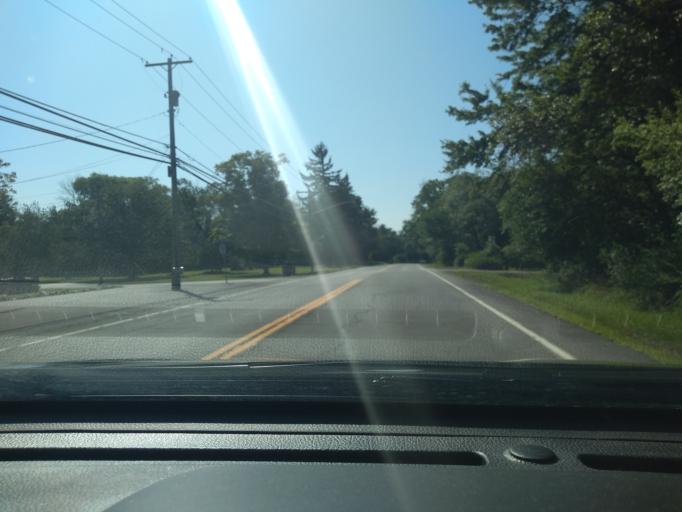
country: US
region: New York
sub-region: Erie County
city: Billington Heights
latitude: 42.7793
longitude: -78.6432
